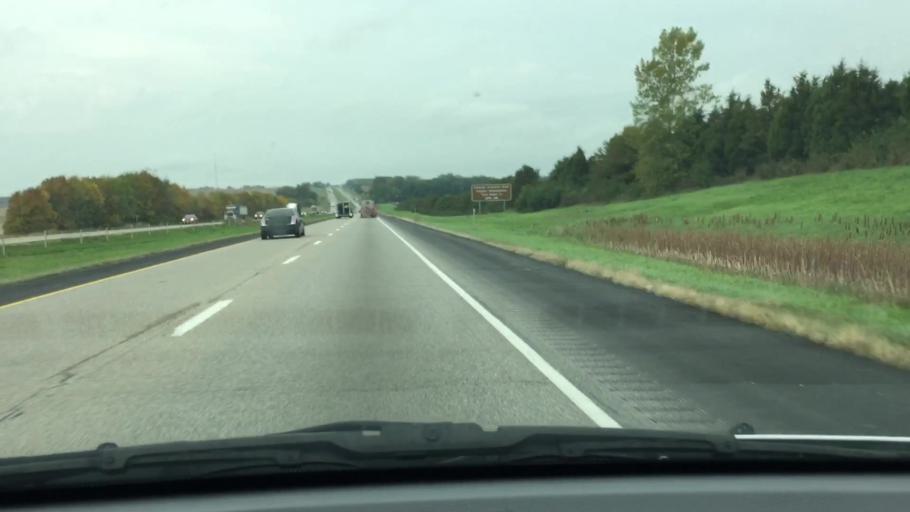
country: US
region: Iowa
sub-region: Cedar County
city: West Branch
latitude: 41.6637
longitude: -91.2744
